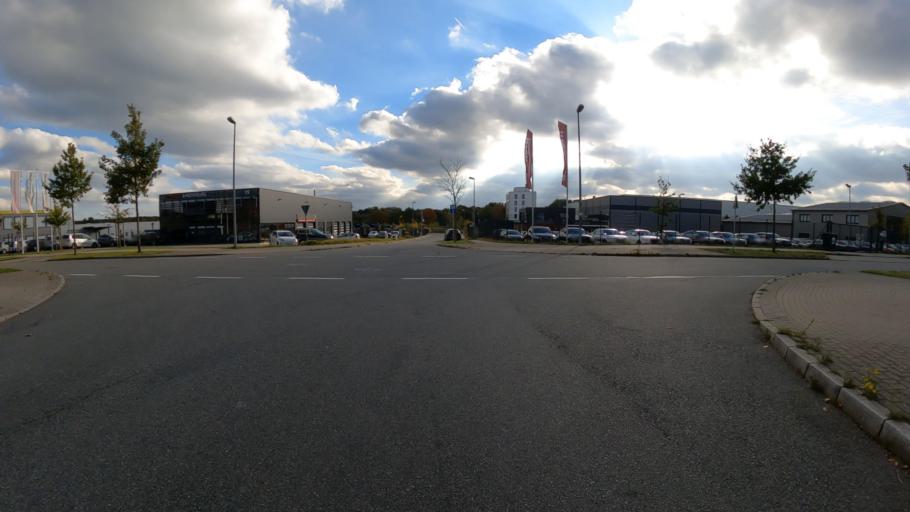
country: DE
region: Schleswig-Holstein
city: Delingsdorf
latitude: 53.6789
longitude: 10.2535
